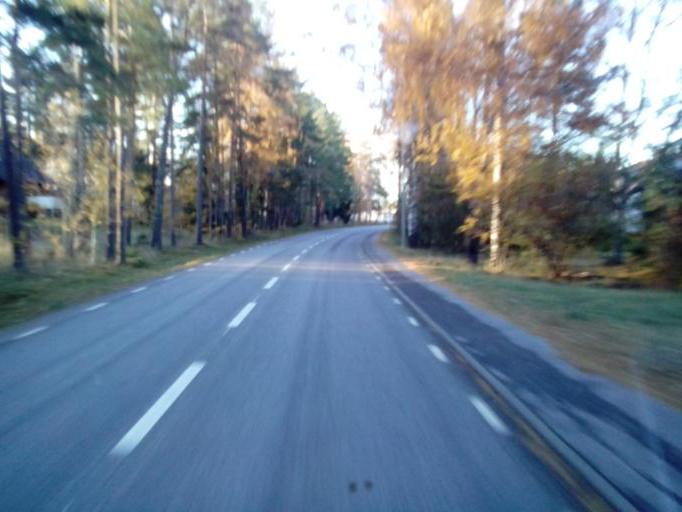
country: SE
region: OErebro
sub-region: Hallsbergs Kommun
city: Palsboda
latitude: 59.0701
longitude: 15.3343
